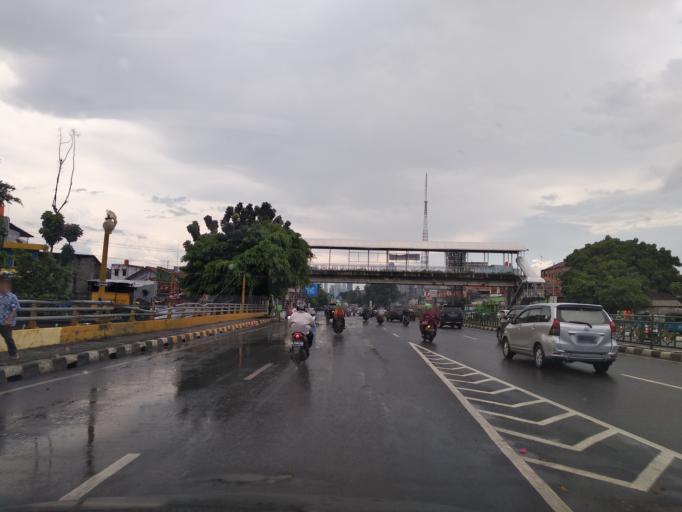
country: ID
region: Jakarta Raya
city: Jakarta
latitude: -6.2251
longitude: 106.8639
